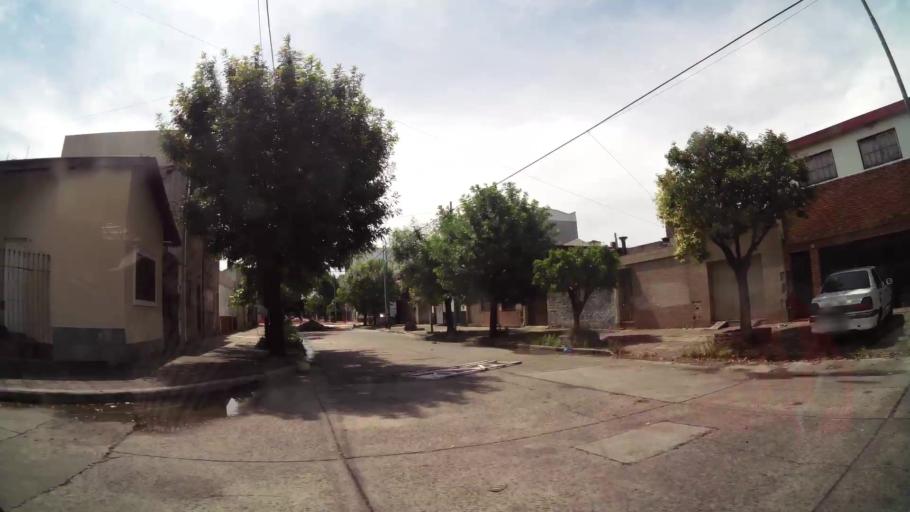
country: AR
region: Buenos Aires F.D.
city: Villa Lugano
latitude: -34.6599
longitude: -58.4380
